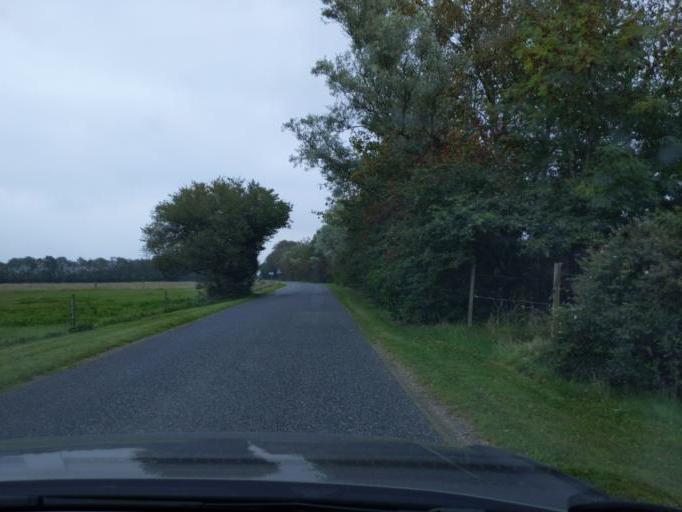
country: DK
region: Central Jutland
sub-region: Viborg Kommune
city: Karup
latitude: 56.3662
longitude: 9.2169
